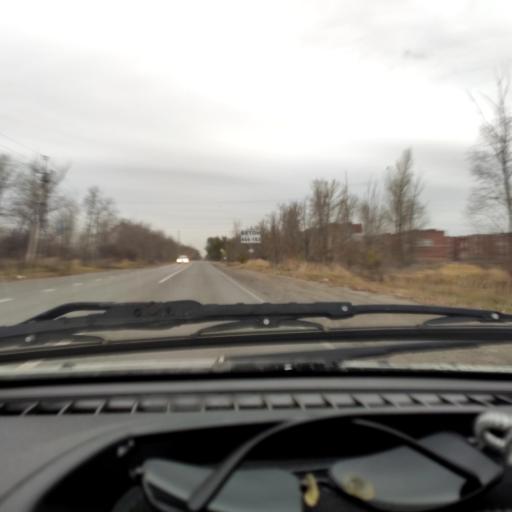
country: RU
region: Samara
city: Tol'yatti
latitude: 53.5428
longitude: 49.3934
